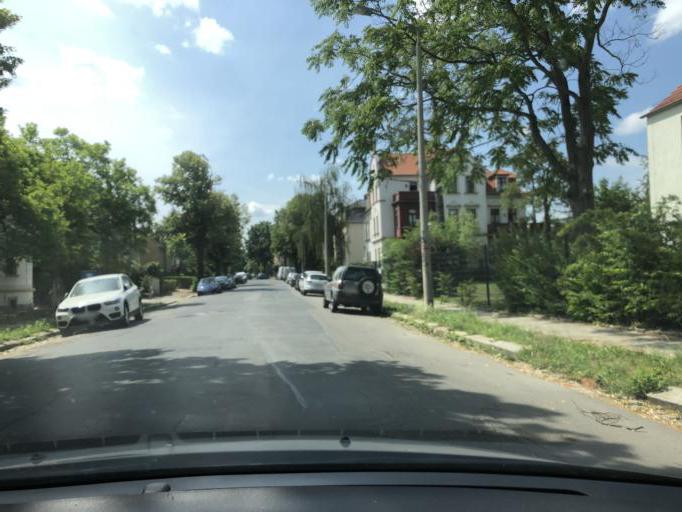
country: DE
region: Saxony
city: Dohna
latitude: 50.9914
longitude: 13.8131
